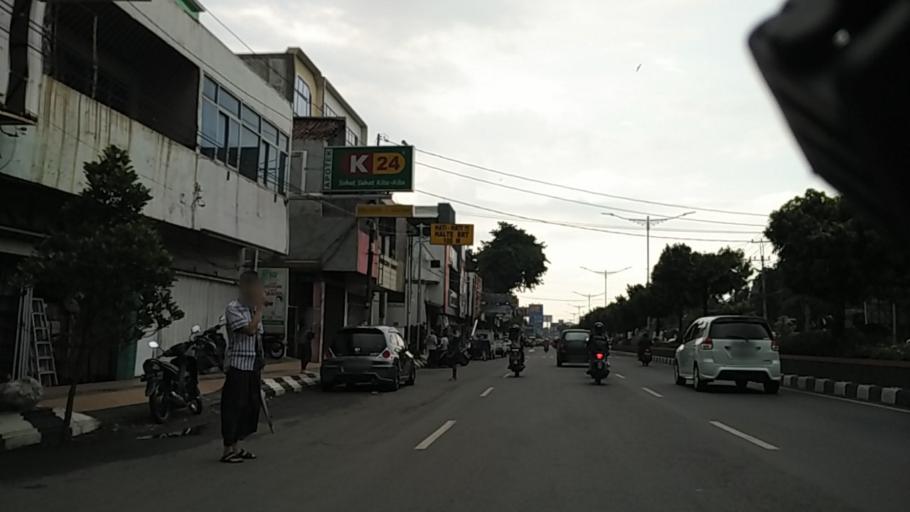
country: ID
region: Central Java
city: Semarang
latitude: -6.9831
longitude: 110.4062
